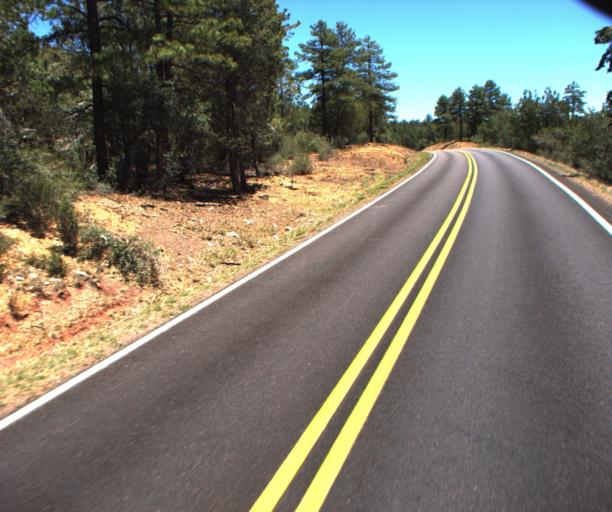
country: US
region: Arizona
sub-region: Gila County
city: Pine
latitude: 34.3643
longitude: -111.4312
